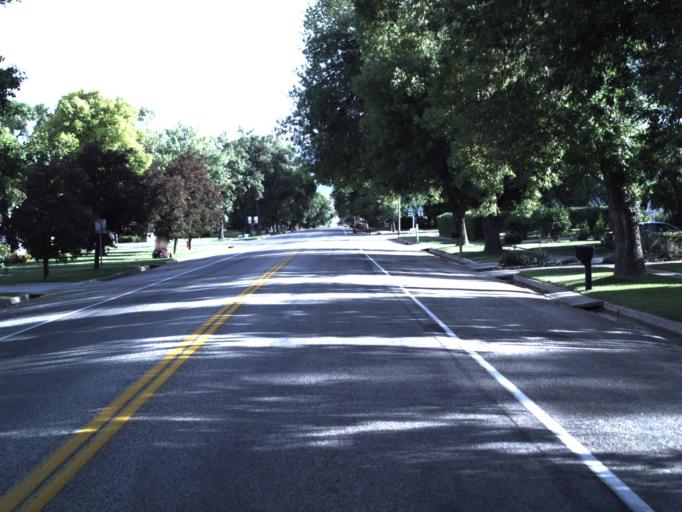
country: US
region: Utah
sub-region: Cache County
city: Wellsville
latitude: 41.6398
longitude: -111.9344
